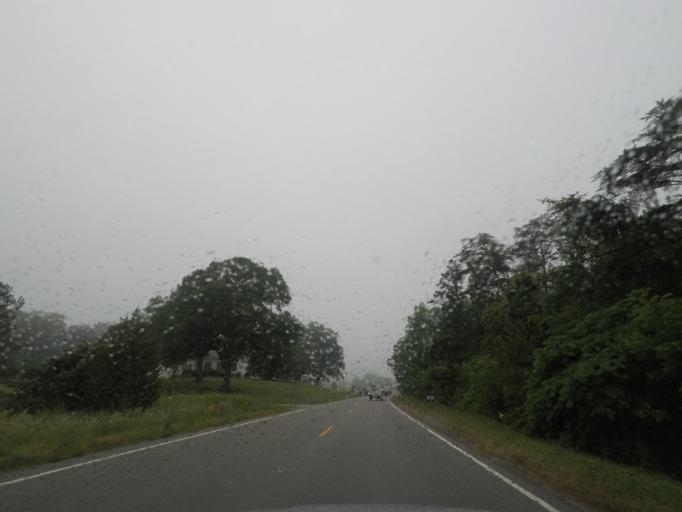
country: US
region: Virginia
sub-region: Prince Edward County
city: Farmville
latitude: 37.3861
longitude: -78.4851
